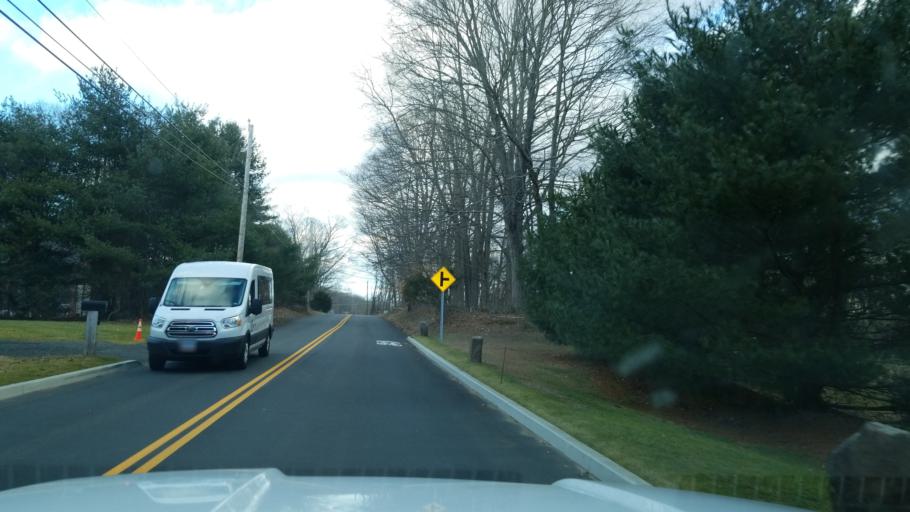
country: US
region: Connecticut
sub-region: Middlesex County
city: Durham
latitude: 41.5088
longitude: -72.6342
